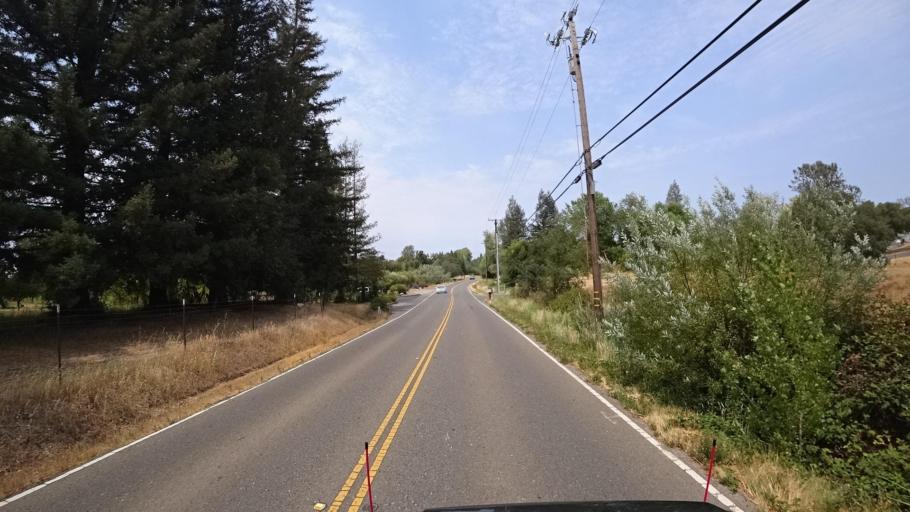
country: US
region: California
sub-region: Placer County
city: Granite Bay
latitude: 38.7811
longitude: -121.1909
